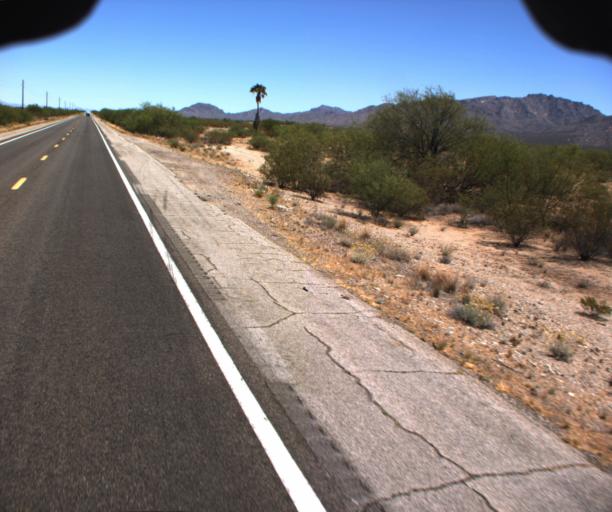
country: US
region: Arizona
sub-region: La Paz County
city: Salome
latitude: 33.8643
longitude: -113.4104
